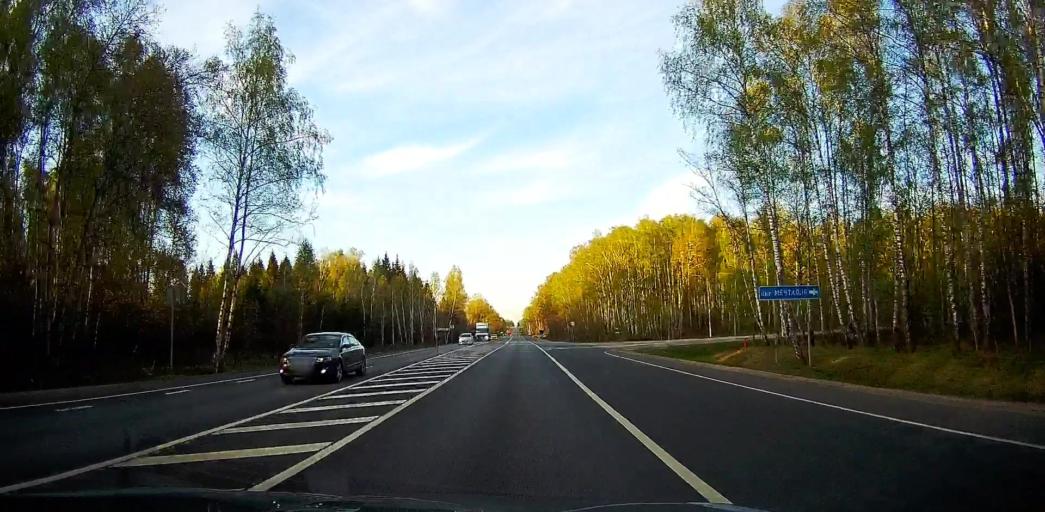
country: RU
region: Moskovskaya
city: Meshcherino
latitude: 55.2342
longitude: 38.4182
